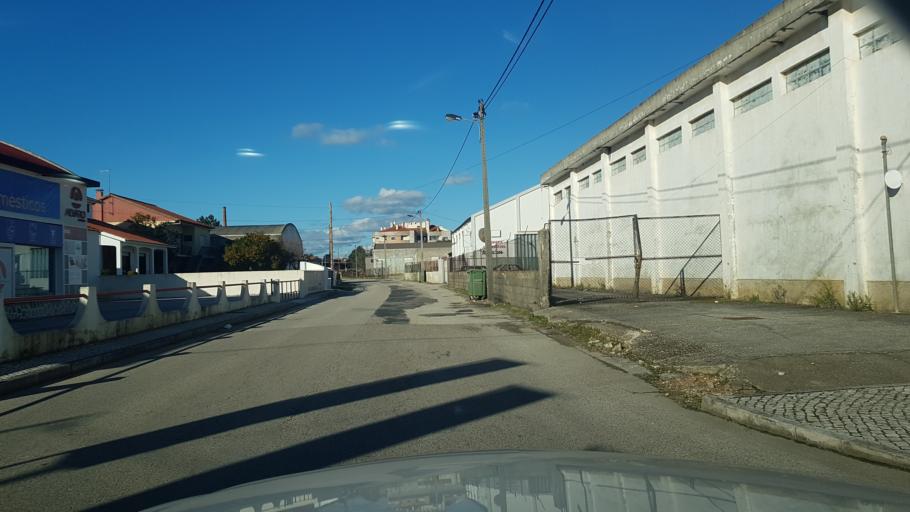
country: PT
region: Santarem
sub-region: Entroncamento
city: Entroncamento
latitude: 39.4750
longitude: -8.4733
